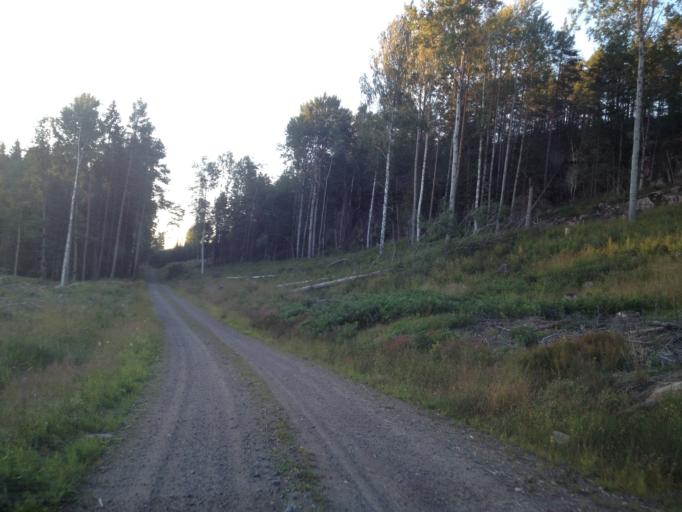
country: SE
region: Kalmar
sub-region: Vasterviks Kommun
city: Overum
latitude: 58.0087
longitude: 16.1227
